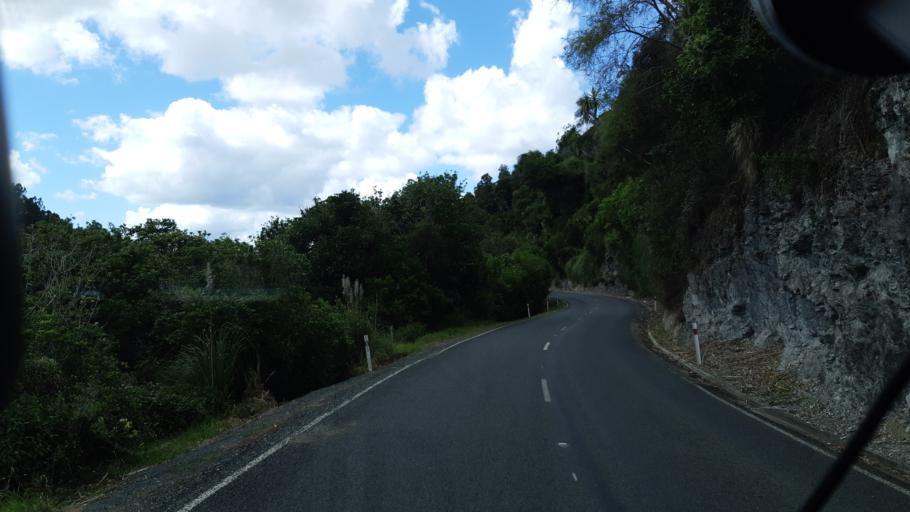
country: NZ
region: Northland
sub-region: Far North District
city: Taipa
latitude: -35.2480
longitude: 173.5304
